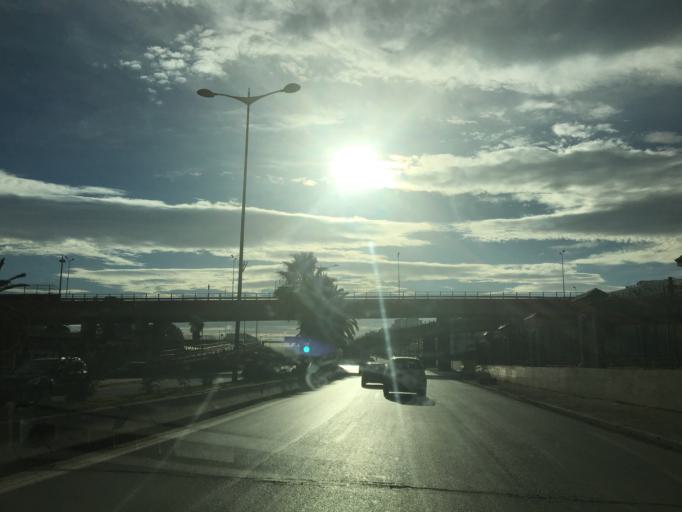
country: DZ
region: Alger
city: Algiers
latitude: 36.7624
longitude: 3.0593
